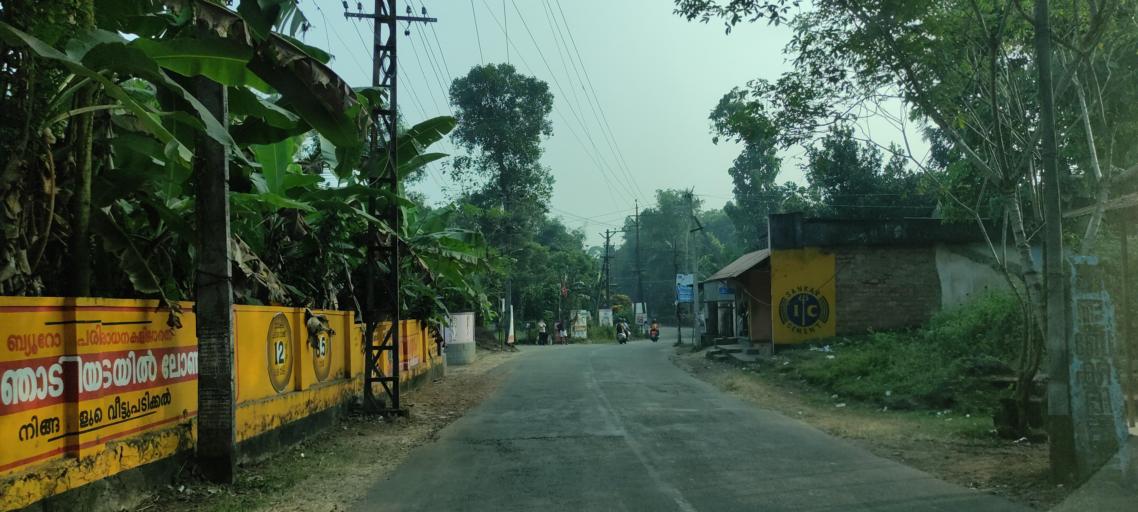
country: IN
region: Kerala
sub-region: Kottayam
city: Vaikam
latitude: 9.7368
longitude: 76.4792
